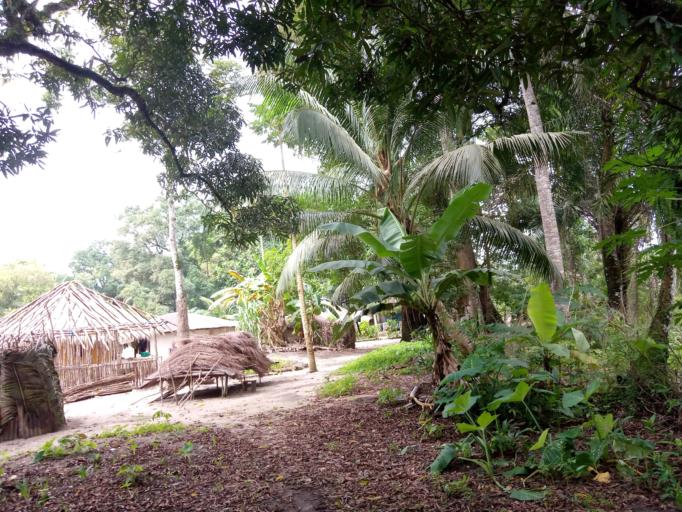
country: SL
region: Southern Province
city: Bonthe
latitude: 7.4773
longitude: -12.5253
